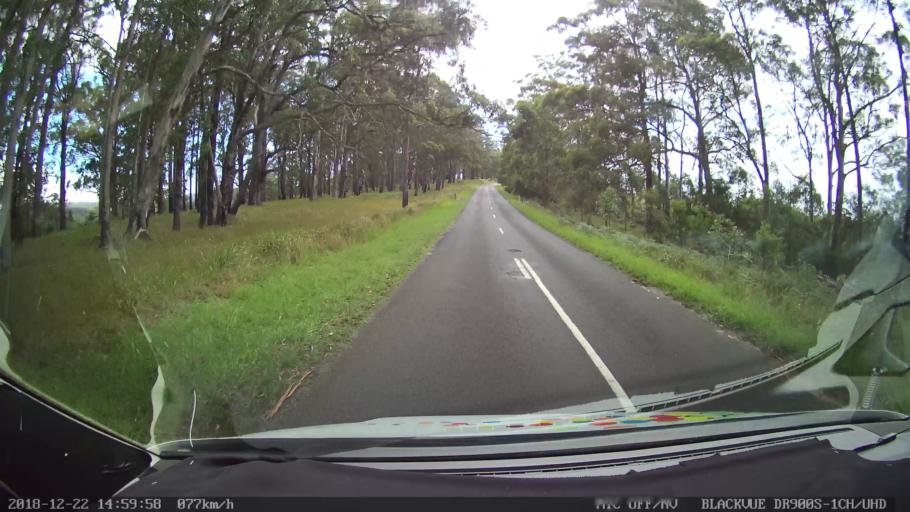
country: AU
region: New South Wales
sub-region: Bellingen
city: Dorrigo
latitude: -30.2495
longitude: 152.4763
